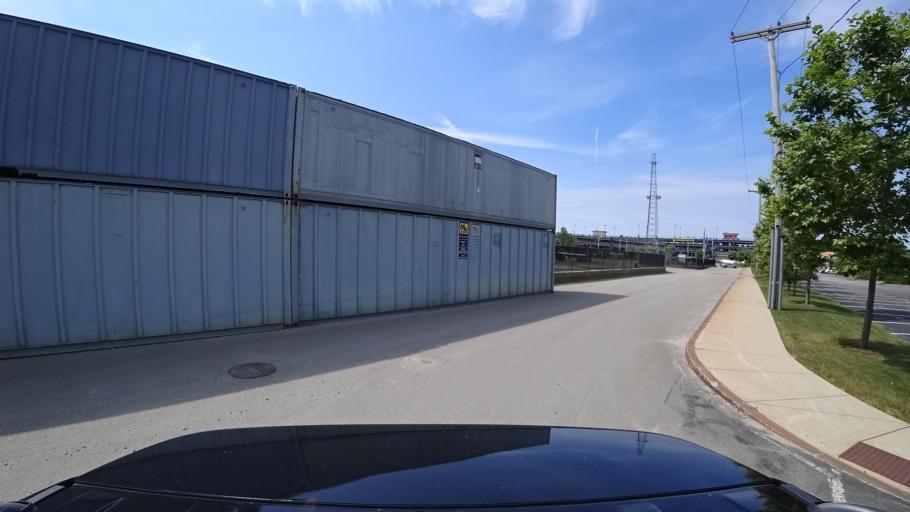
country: US
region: Massachusetts
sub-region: Norfolk County
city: Dedham
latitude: 42.2334
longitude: -71.1749
